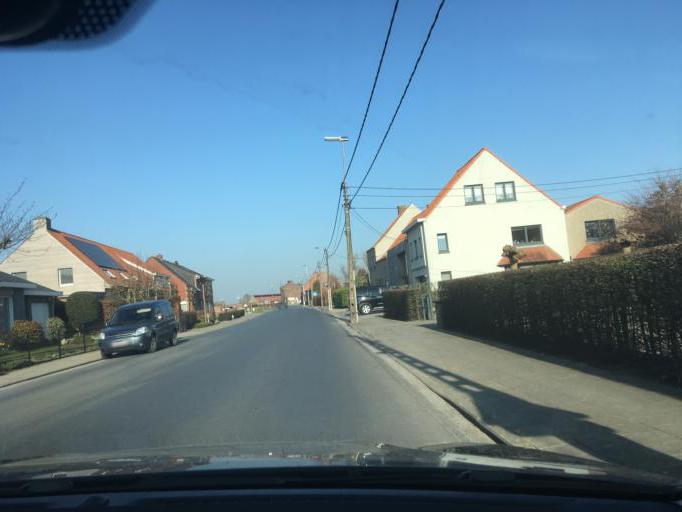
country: BE
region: Flanders
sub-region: Provincie West-Vlaanderen
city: Ledegem
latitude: 50.8627
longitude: 3.1373
